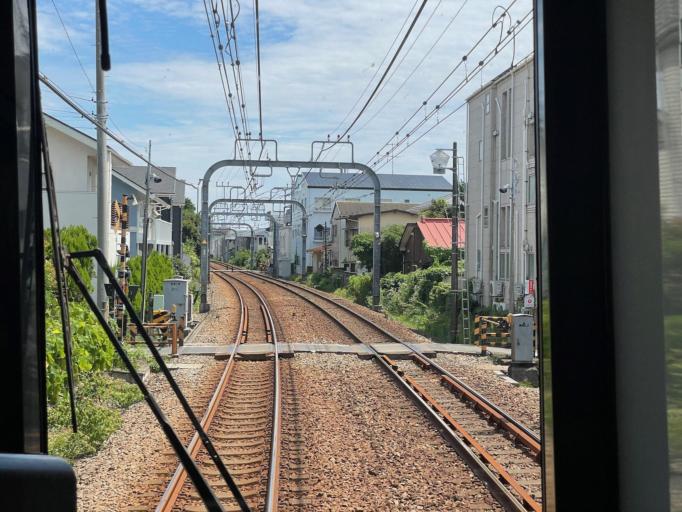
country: JP
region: Kanagawa
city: Fujisawa
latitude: 35.3171
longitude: 139.4750
